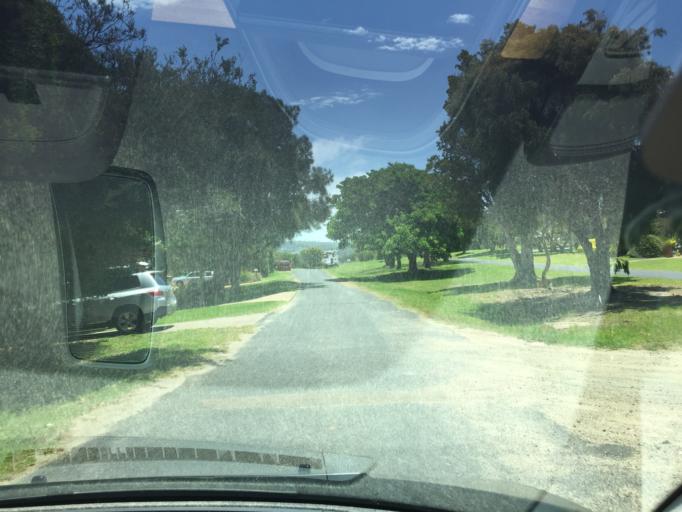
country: AU
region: New South Wales
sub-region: Bega Valley
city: Merimbula
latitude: -36.8953
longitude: 149.9268
